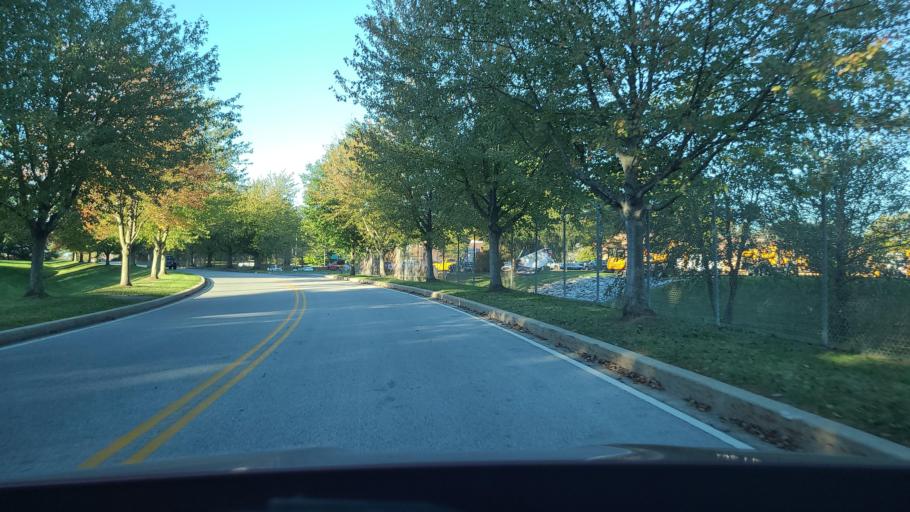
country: US
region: Maryland
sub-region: Carroll County
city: Westminster
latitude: 39.5935
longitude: -77.0015
